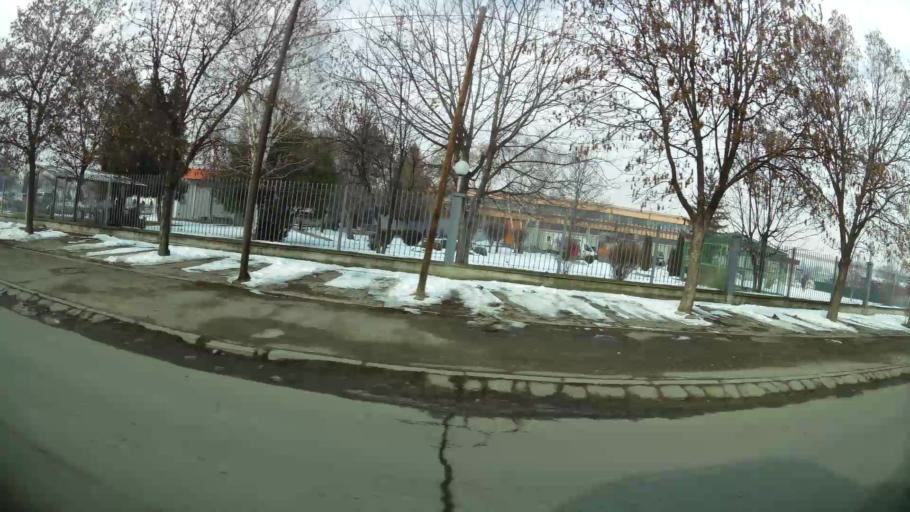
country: MK
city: Krushopek
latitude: 42.0152
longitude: 21.3642
